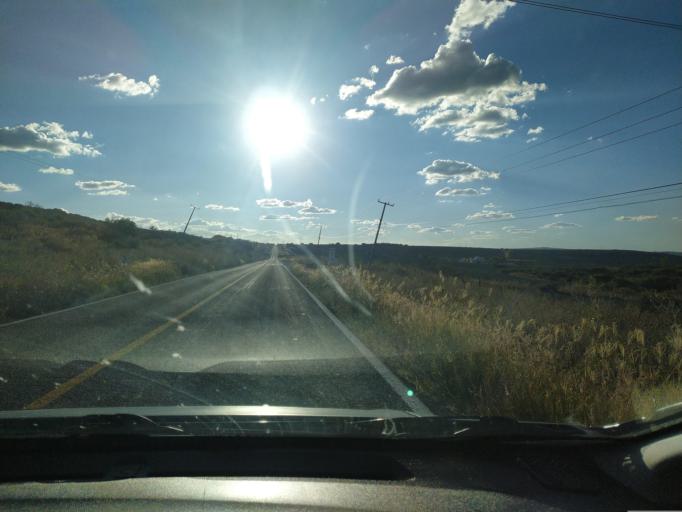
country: MX
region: Guanajuato
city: San Francisco del Rincon
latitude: 21.0336
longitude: -101.9179
